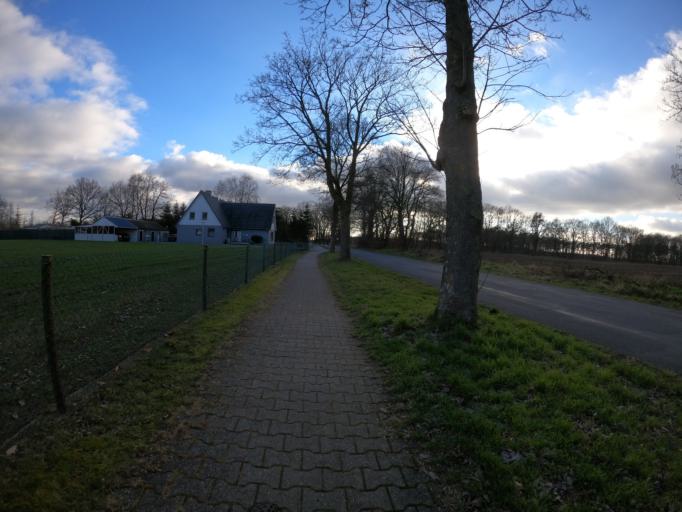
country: DE
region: Lower Saxony
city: Bawinkel
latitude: 52.6678
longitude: 7.3921
